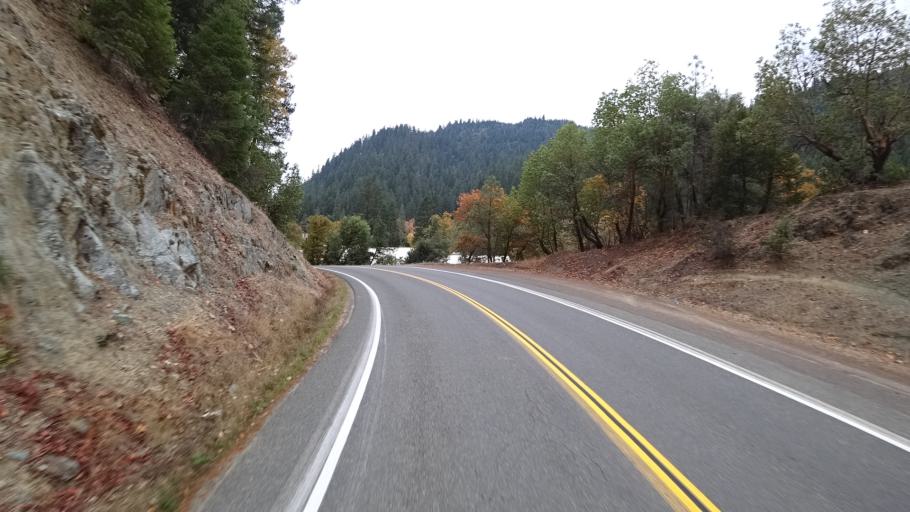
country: US
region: California
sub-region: Siskiyou County
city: Happy Camp
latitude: 41.8410
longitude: -123.3836
